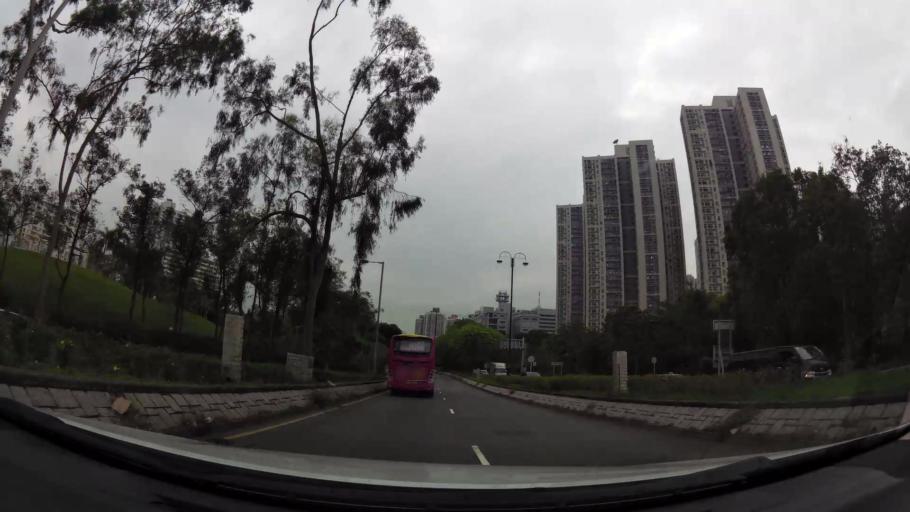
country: HK
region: Tai Po
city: Tai Po
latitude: 22.4509
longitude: 114.1768
